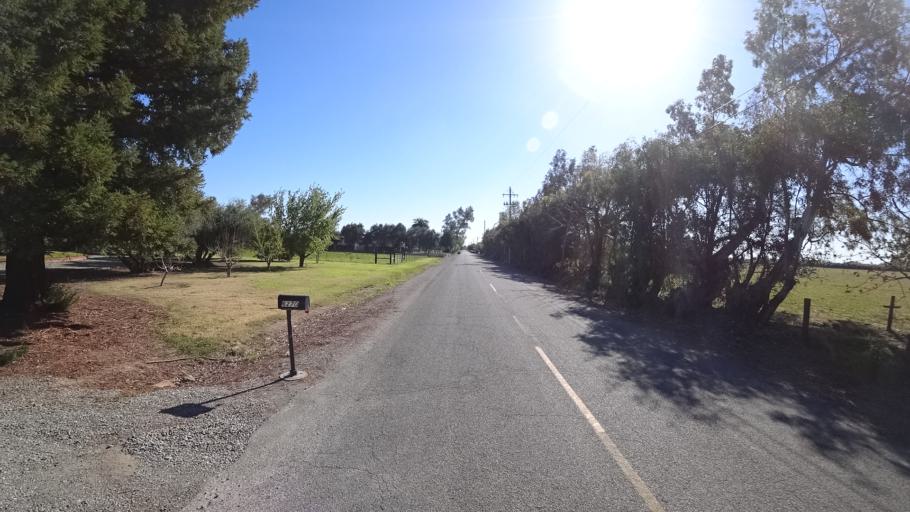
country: US
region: California
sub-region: Glenn County
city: Orland
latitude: 39.7440
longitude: -122.2231
